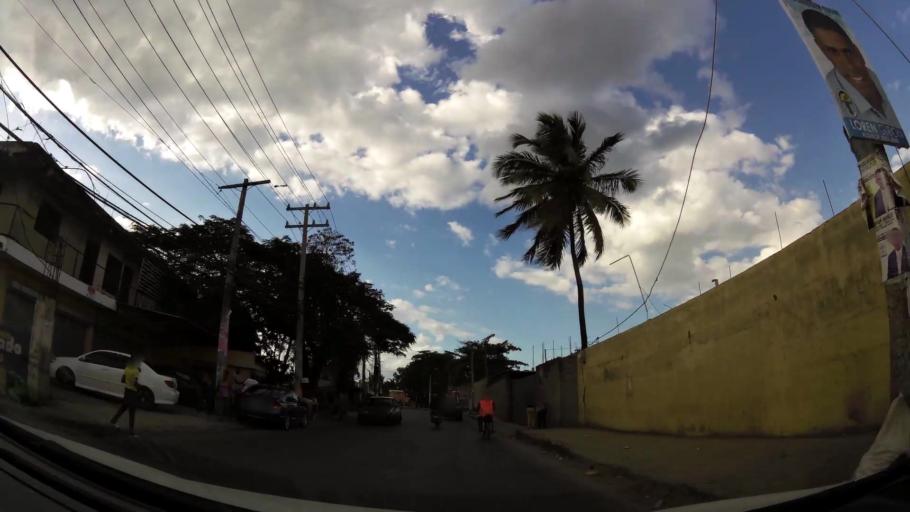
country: DO
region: Nacional
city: Ensanche Luperon
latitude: 18.5627
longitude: -69.9059
